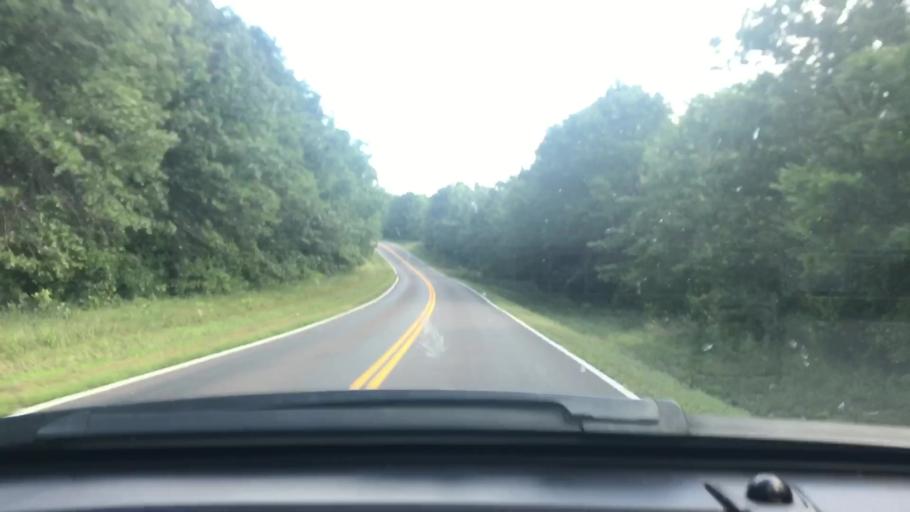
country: US
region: Missouri
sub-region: Wright County
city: Hartville
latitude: 37.3541
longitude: -92.3403
